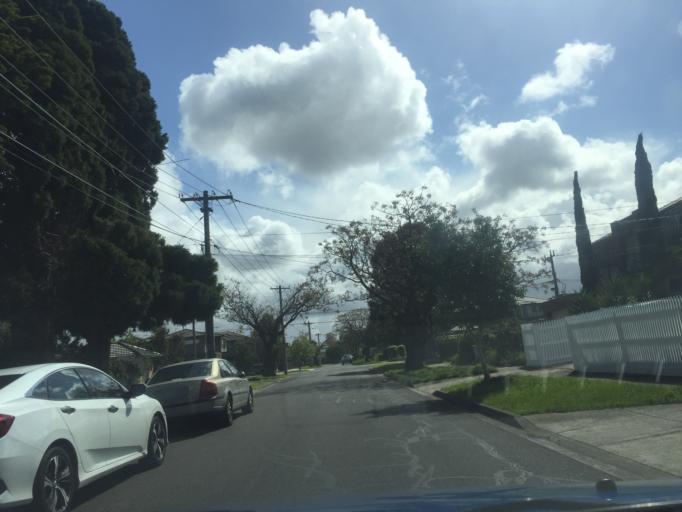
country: AU
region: Victoria
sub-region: Banyule
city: Bellfield
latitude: -37.7578
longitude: 145.0359
